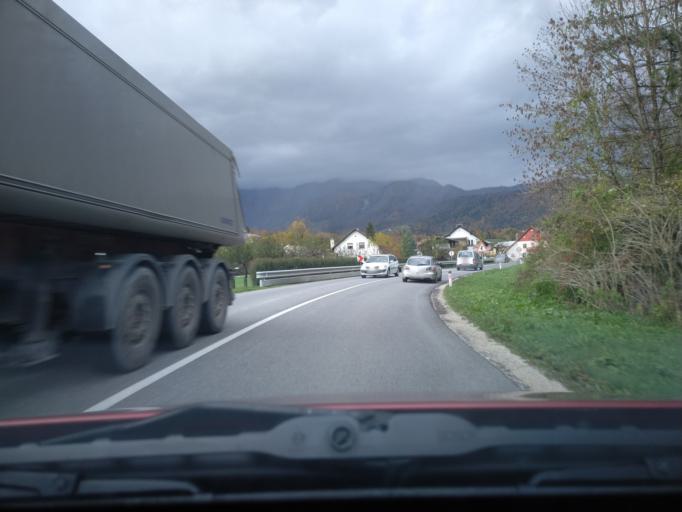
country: SI
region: Kamnik
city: Mekinje
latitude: 46.2456
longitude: 14.6018
